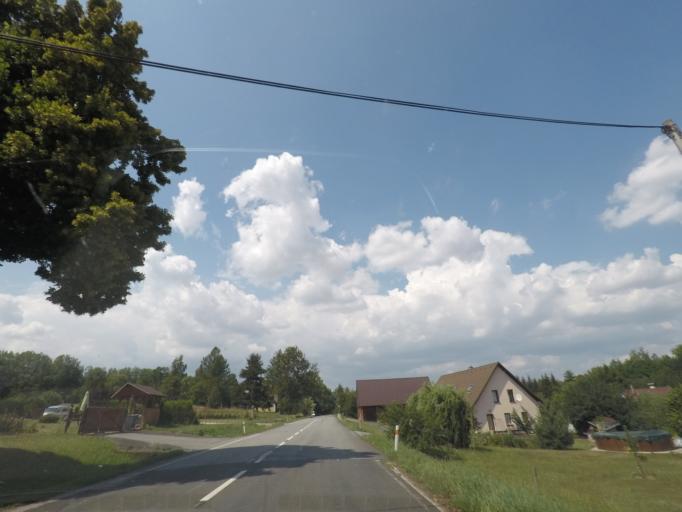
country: CZ
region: Kralovehradecky
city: Zadni Mostek
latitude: 50.5270
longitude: 15.6867
